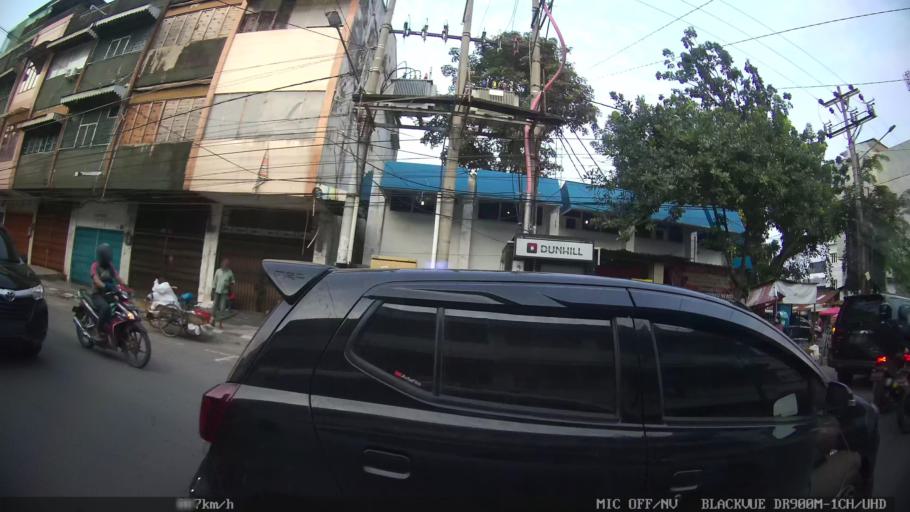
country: ID
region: North Sumatra
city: Medan
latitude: 3.5937
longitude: 98.6892
